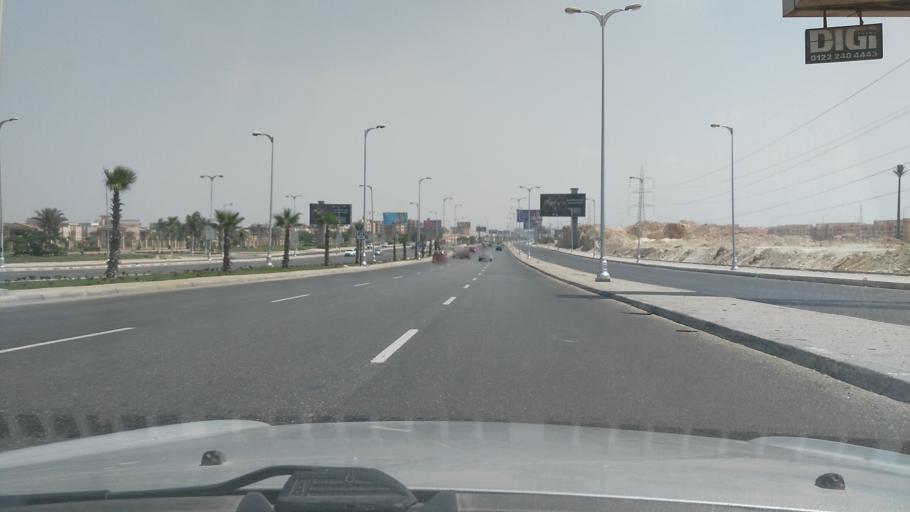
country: EG
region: Al Jizah
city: Awsim
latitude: 30.0349
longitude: 31.0324
